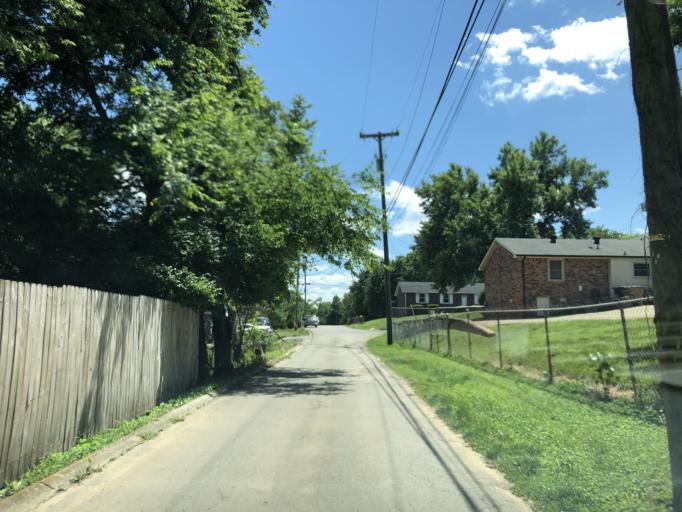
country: US
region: Tennessee
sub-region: Davidson County
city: Nashville
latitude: 36.1883
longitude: -86.7223
